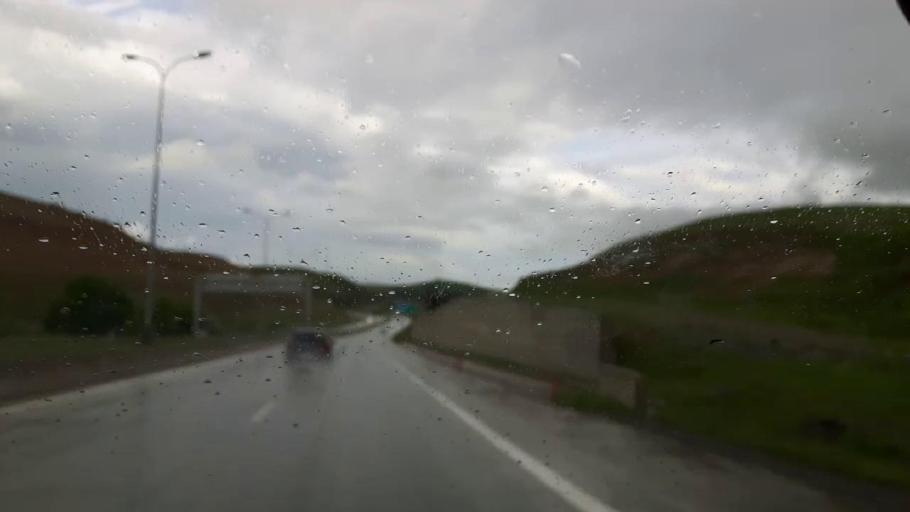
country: GE
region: Shida Kartli
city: Kaspi
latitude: 41.9987
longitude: 44.3961
